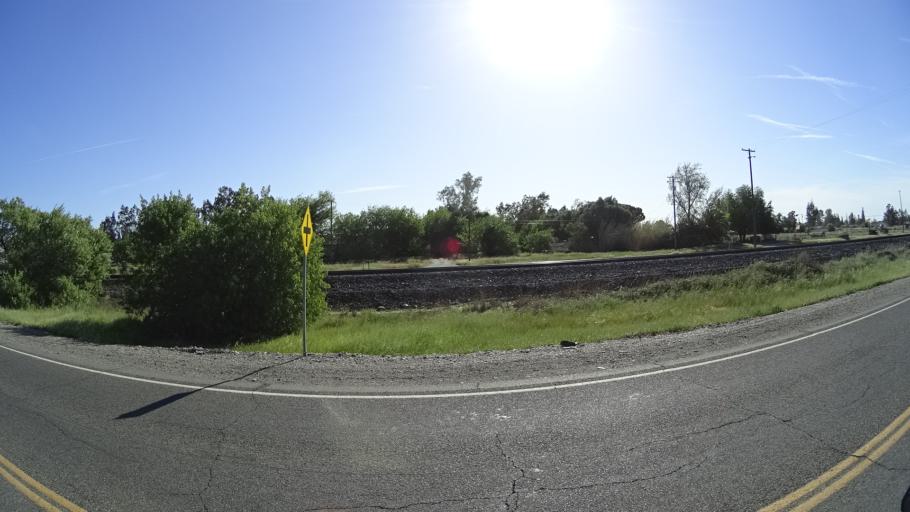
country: US
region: California
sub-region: Glenn County
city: Orland
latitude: 39.7312
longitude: -122.1967
